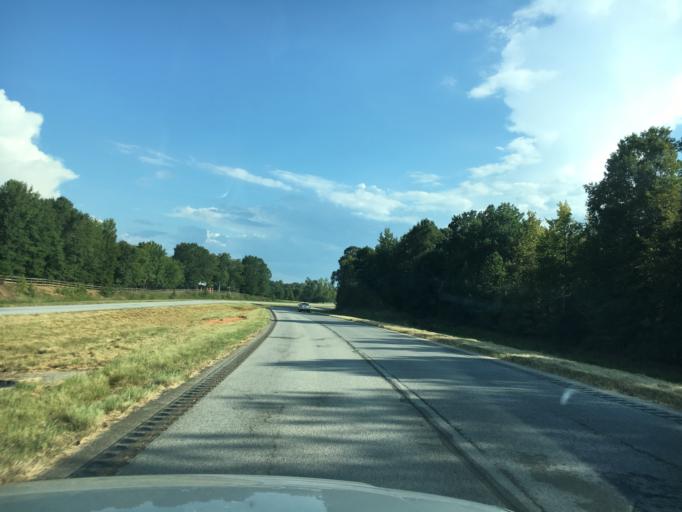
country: US
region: South Carolina
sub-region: Laurens County
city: Clinton
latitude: 34.3563
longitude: -81.9668
